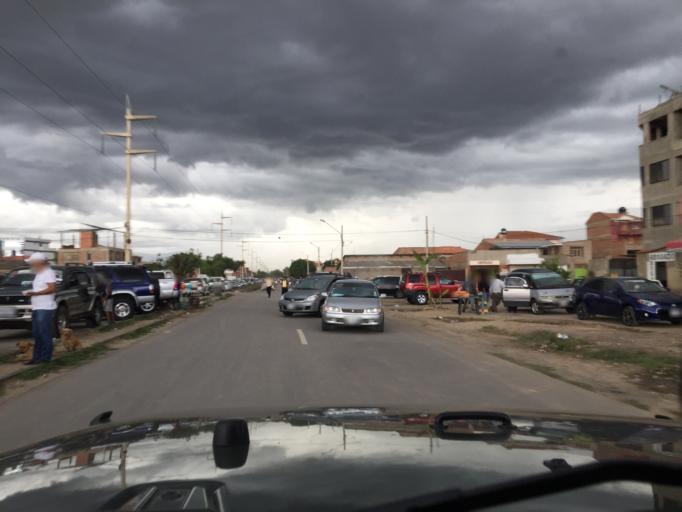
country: BO
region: Cochabamba
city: Cochabamba
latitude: -17.4004
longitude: -66.1888
